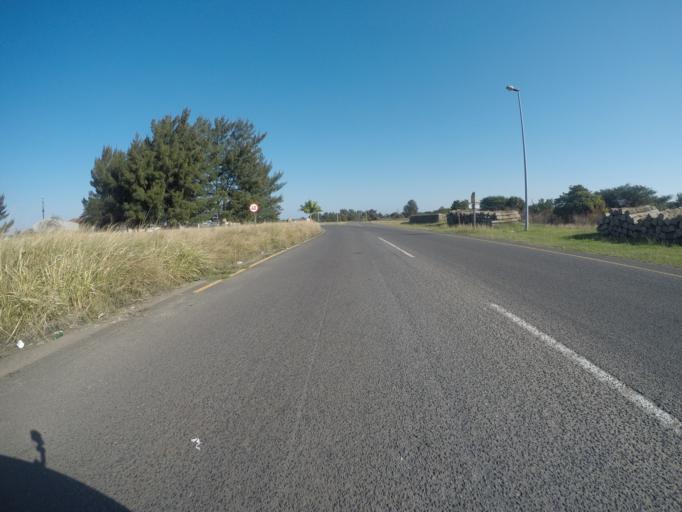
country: ZA
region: KwaZulu-Natal
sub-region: uThungulu District Municipality
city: Richards Bay
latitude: -28.7910
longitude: 32.0777
